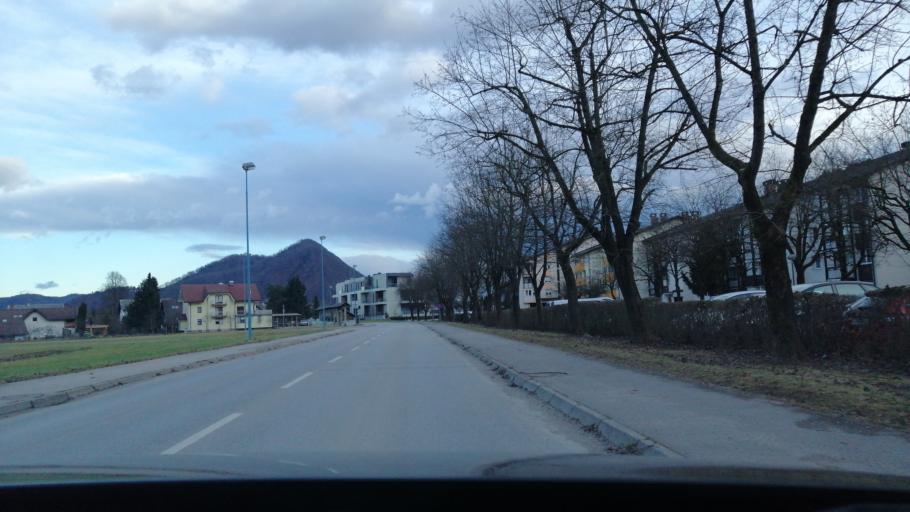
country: SI
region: Medvode
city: Medvode
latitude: 46.1344
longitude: 14.4129
